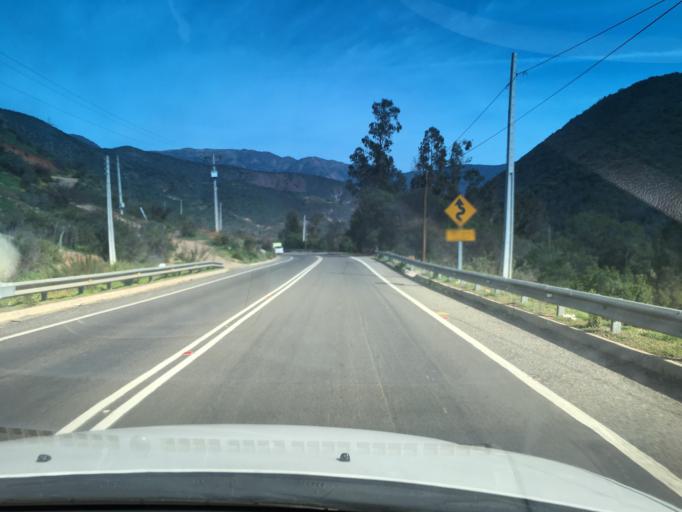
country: CL
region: Valparaiso
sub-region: Provincia de Marga Marga
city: Limache
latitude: -33.0597
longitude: -71.0554
